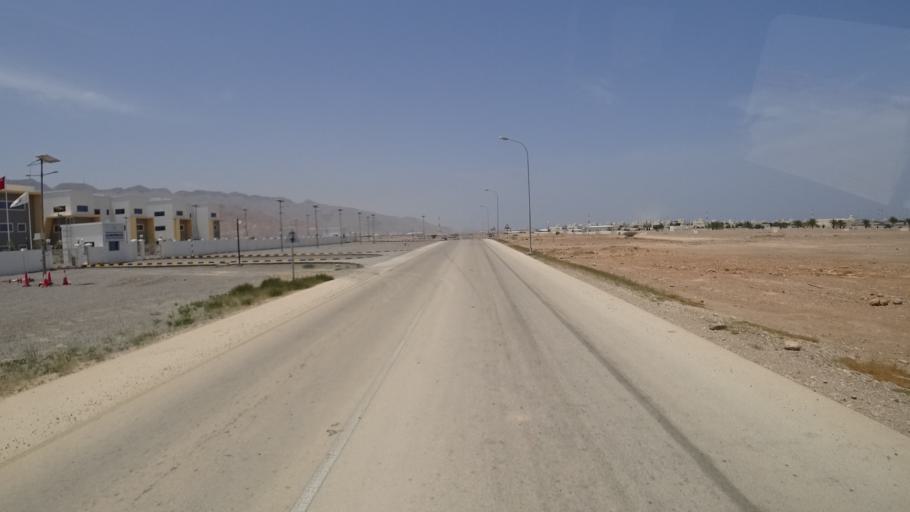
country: OM
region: Ash Sharqiyah
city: Sur
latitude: 22.6006
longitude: 59.4387
